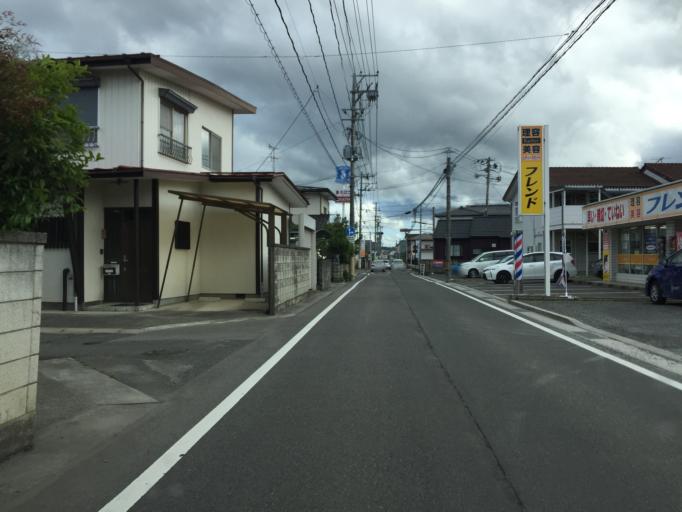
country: JP
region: Fukushima
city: Fukushima-shi
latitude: 37.7687
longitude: 140.4441
